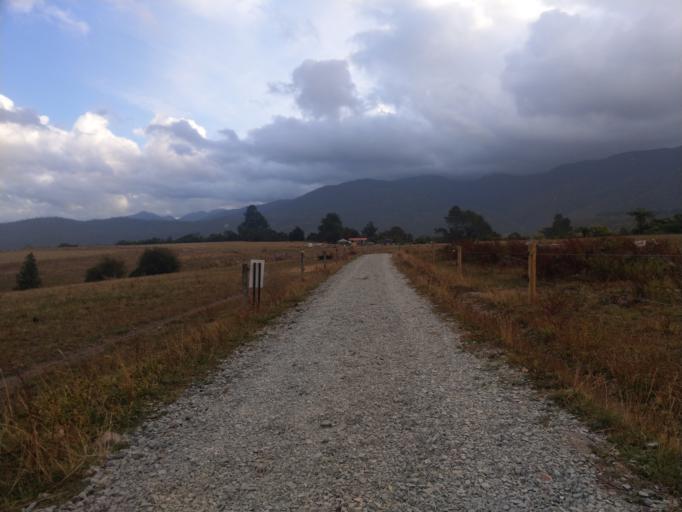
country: NZ
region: Tasman
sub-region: Tasman District
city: Takaka
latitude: -40.7908
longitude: 172.7443
